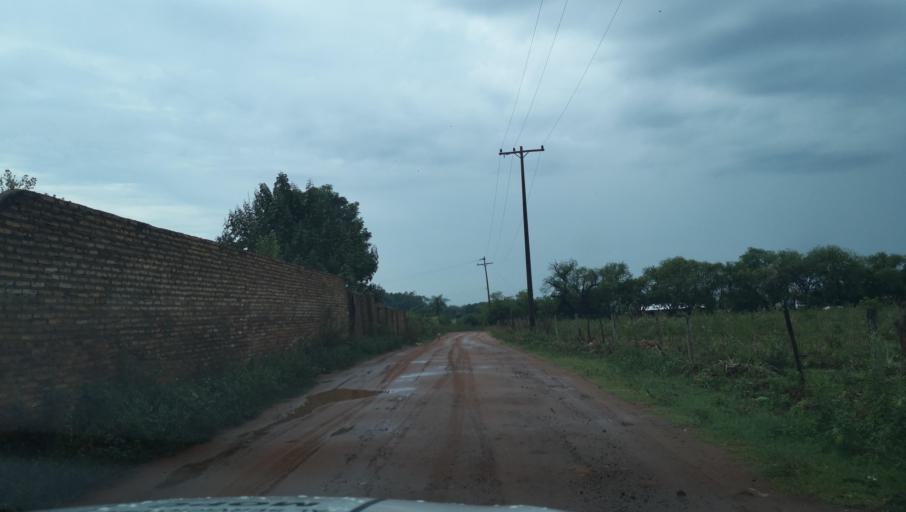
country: PY
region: Misiones
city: Santa Maria
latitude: -26.9015
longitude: -57.0347
